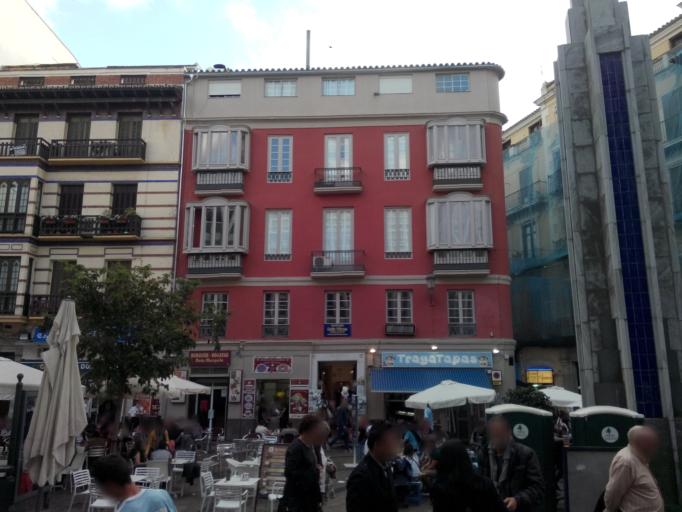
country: ES
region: Andalusia
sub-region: Provincia de Malaga
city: Malaga
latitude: 36.7227
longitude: -4.4204
